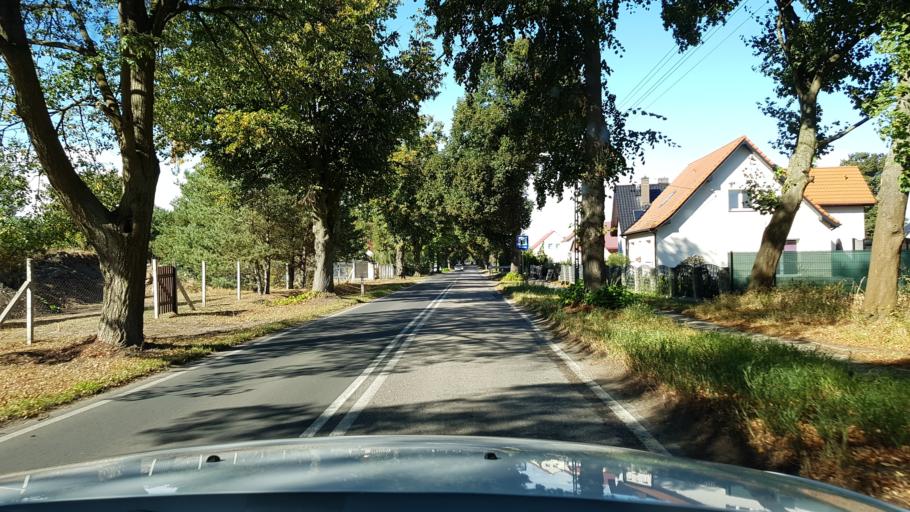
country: PL
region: West Pomeranian Voivodeship
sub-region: Powiat gryfinski
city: Gryfino
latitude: 53.2114
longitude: 14.4996
